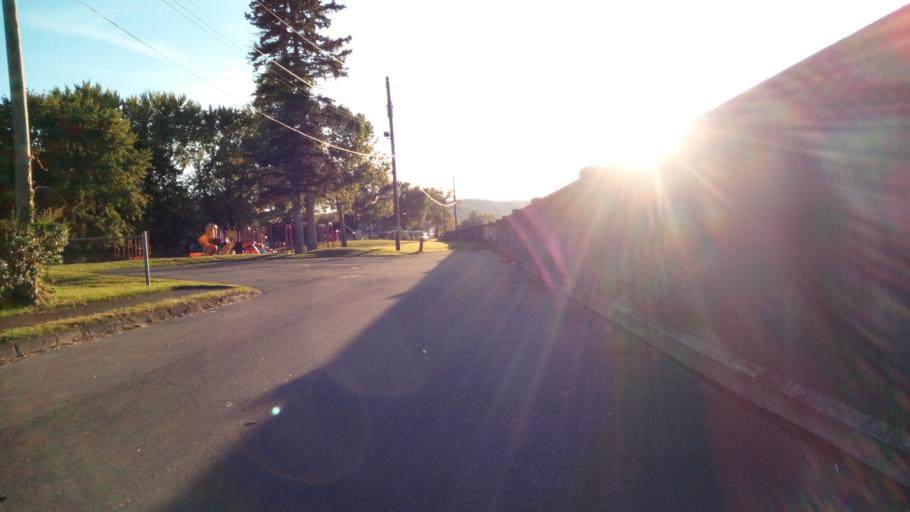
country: US
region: New York
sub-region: Chemung County
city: Elmira
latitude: 42.0840
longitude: -76.8102
